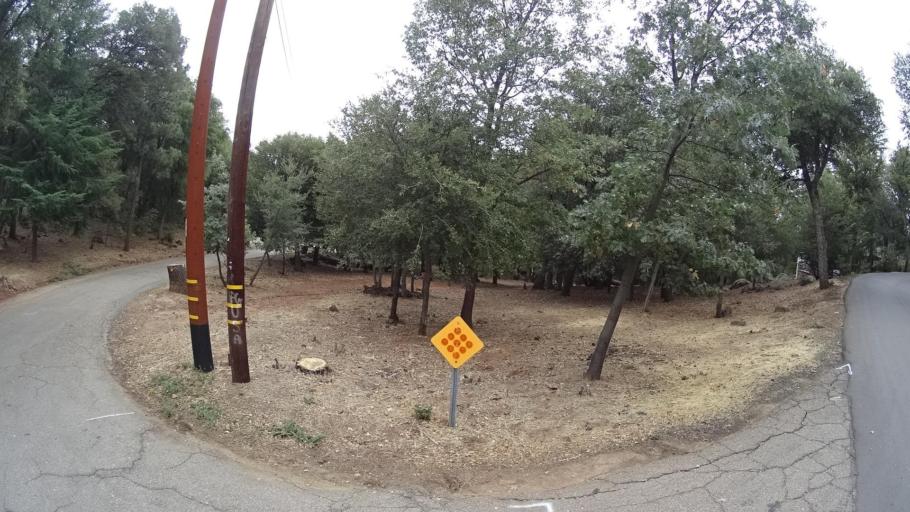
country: US
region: California
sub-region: San Diego County
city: Julian
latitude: 33.0476
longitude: -116.6319
